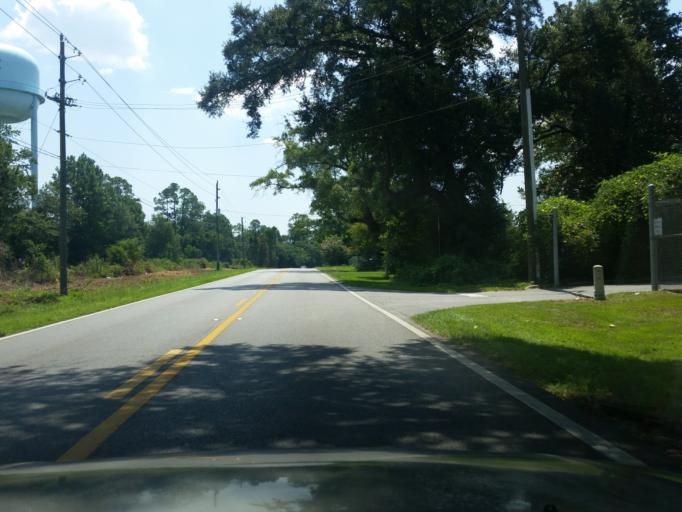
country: US
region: Florida
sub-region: Escambia County
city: Gonzalez
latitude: 30.5843
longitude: -87.2983
